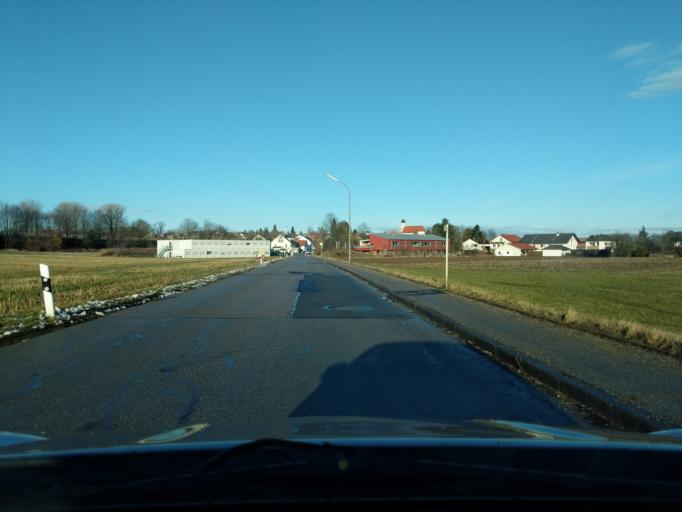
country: DE
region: Bavaria
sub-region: Upper Bavaria
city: Zorneding
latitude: 48.0919
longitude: 11.8396
